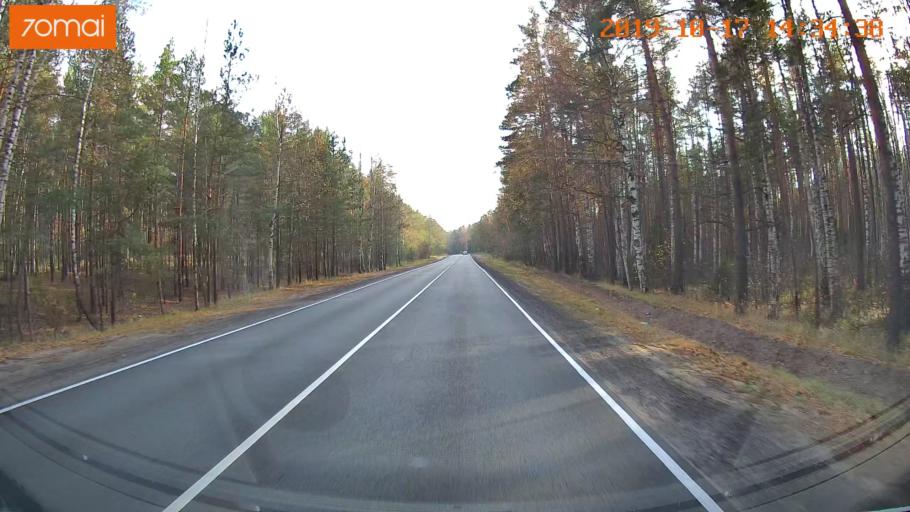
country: RU
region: Rjazan
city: Solotcha
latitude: 54.9098
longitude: 39.9983
